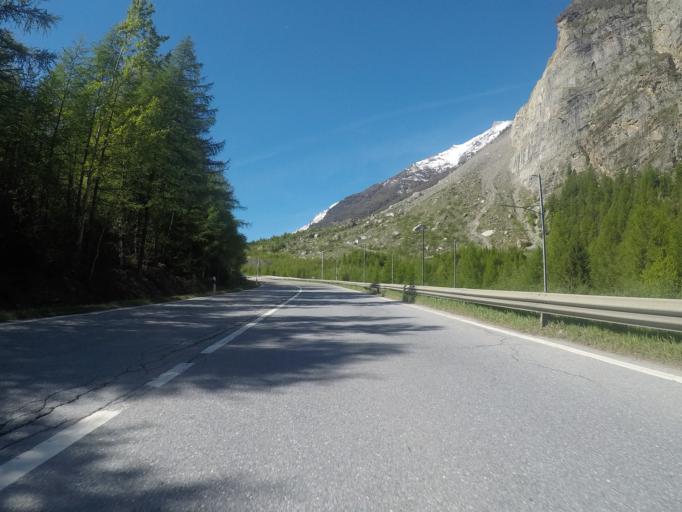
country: CH
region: Valais
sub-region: Visp District
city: Sankt Niklaus
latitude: 46.1178
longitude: 7.7869
